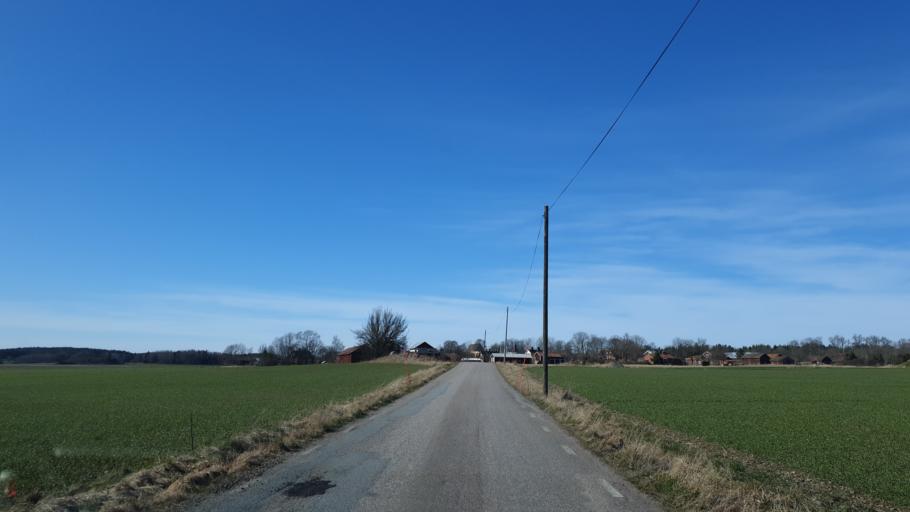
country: SE
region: Uppsala
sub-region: Enkopings Kommun
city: Dalby
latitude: 59.5201
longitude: 17.2813
